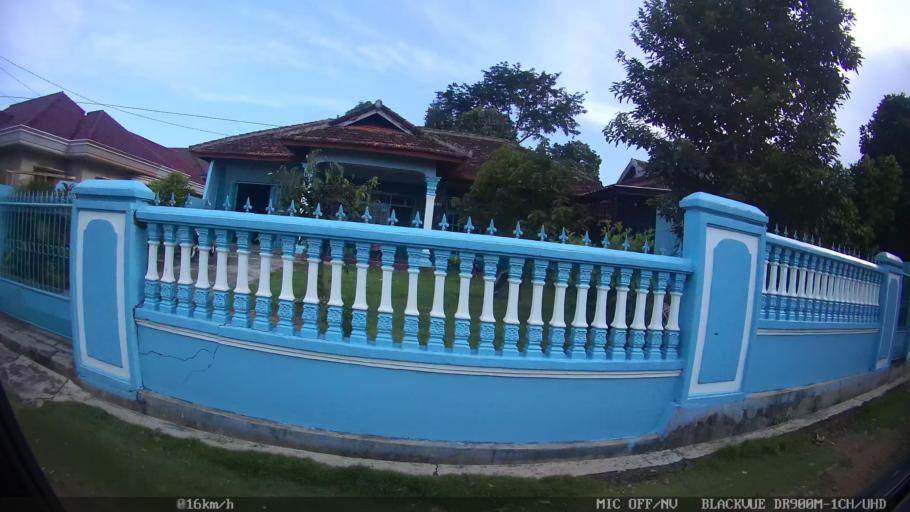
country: ID
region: Lampung
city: Kedaton
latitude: -5.3799
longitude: 105.2315
